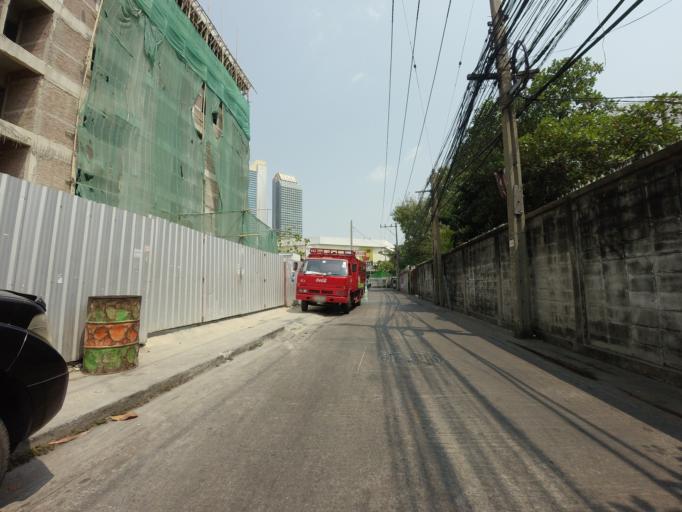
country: TH
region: Bangkok
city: Huai Khwang
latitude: 13.7693
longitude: 100.5696
